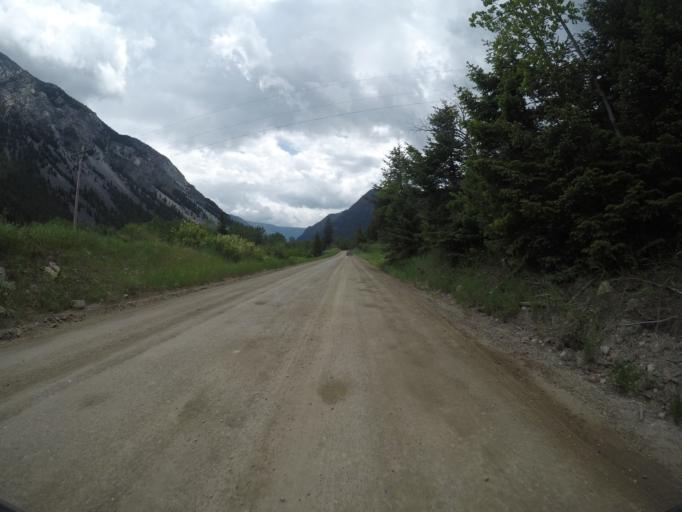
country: US
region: Montana
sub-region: Park County
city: Livingston
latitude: 45.5080
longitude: -110.2270
